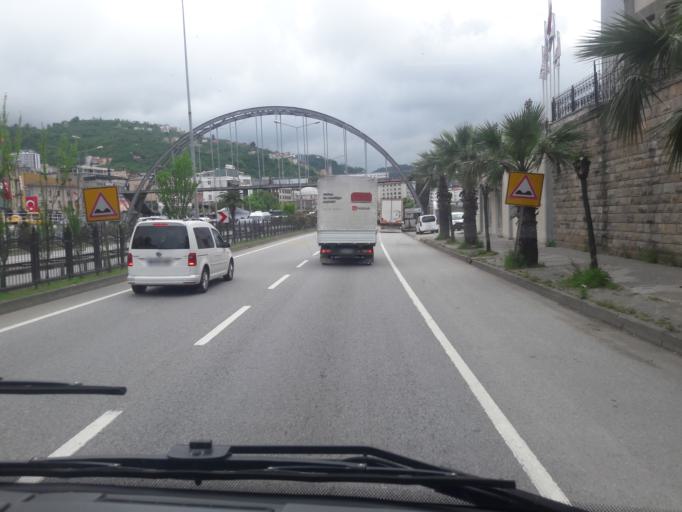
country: TR
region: Giresun
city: Giresun
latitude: 40.9190
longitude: 38.3847
